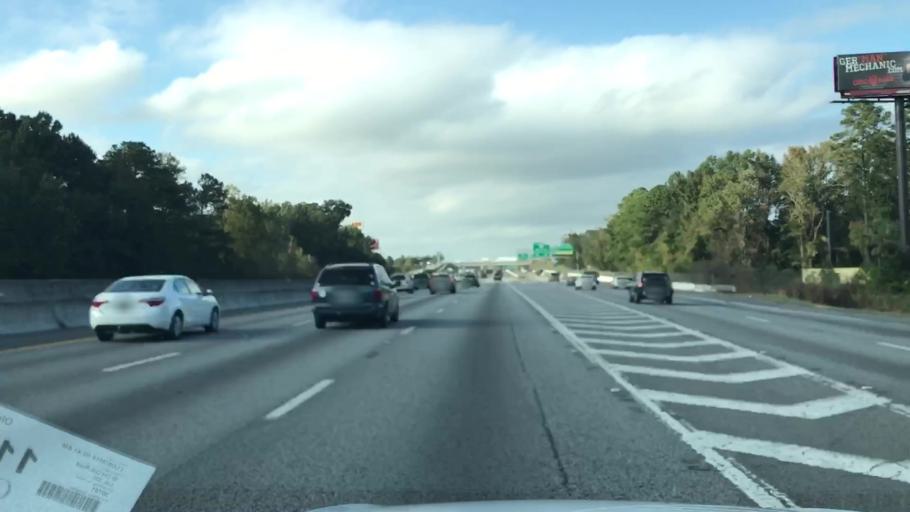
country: US
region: South Carolina
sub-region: Berkeley County
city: Hanahan
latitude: 32.9292
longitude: -80.0444
